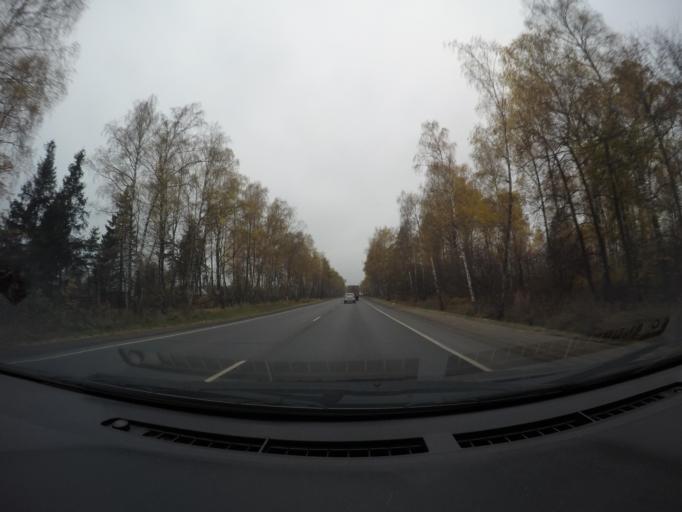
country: RU
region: Moskovskaya
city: Malyshevo
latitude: 55.4883
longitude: 38.3581
